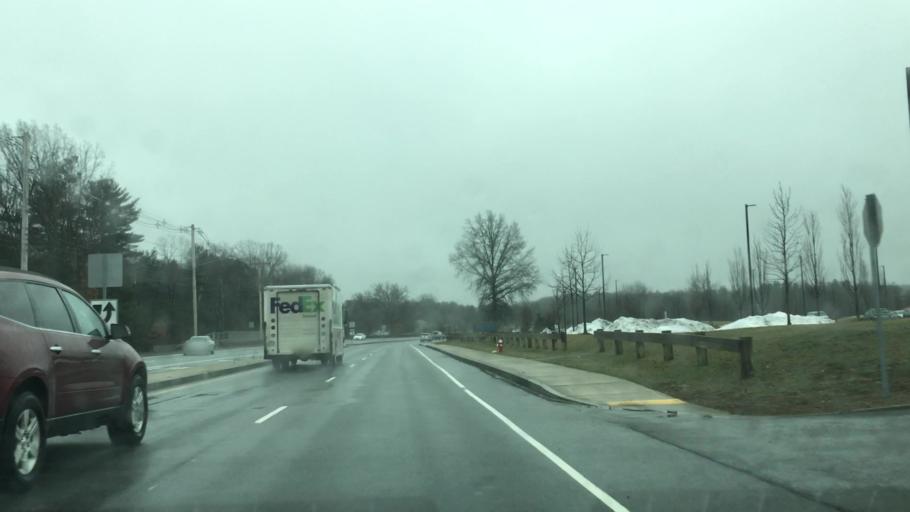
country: US
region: Massachusetts
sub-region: Middlesex County
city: Pinehurst
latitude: 42.5072
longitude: -71.2329
